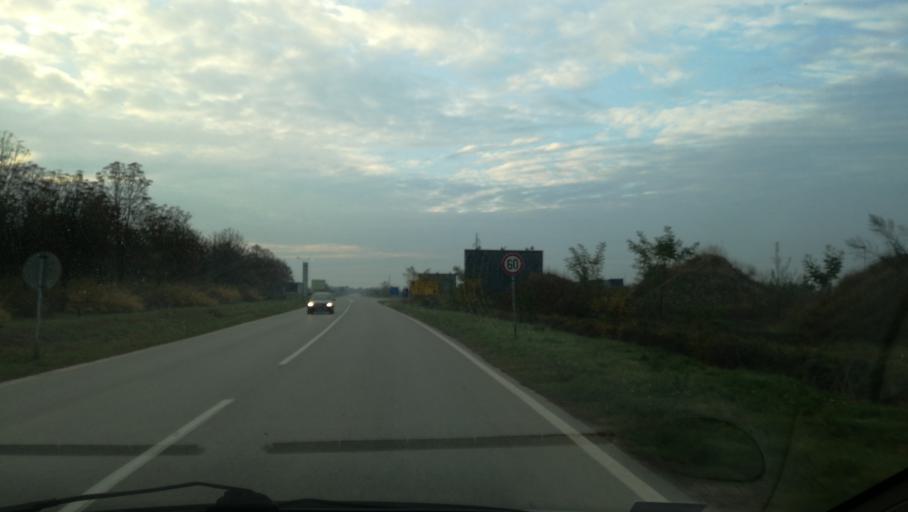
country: RS
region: Autonomna Pokrajina Vojvodina
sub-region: Severnobanatski Okrug
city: Kikinda
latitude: 45.8079
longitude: 20.4333
